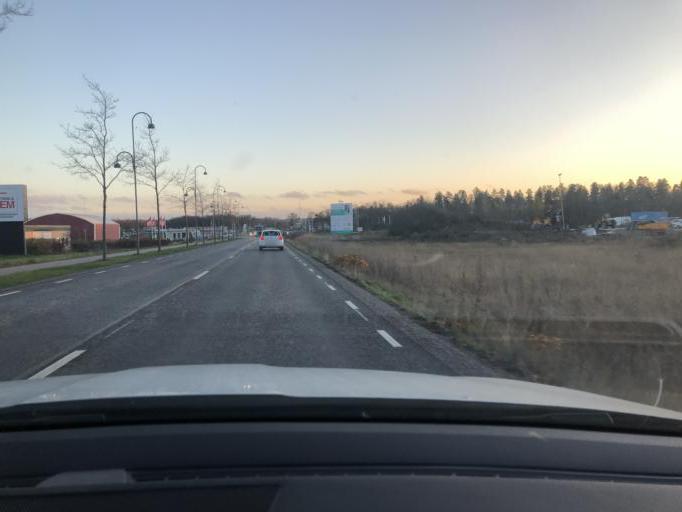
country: SE
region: Soedermanland
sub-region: Strangnas Kommun
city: Strangnas
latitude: 59.3559
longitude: 17.0280
